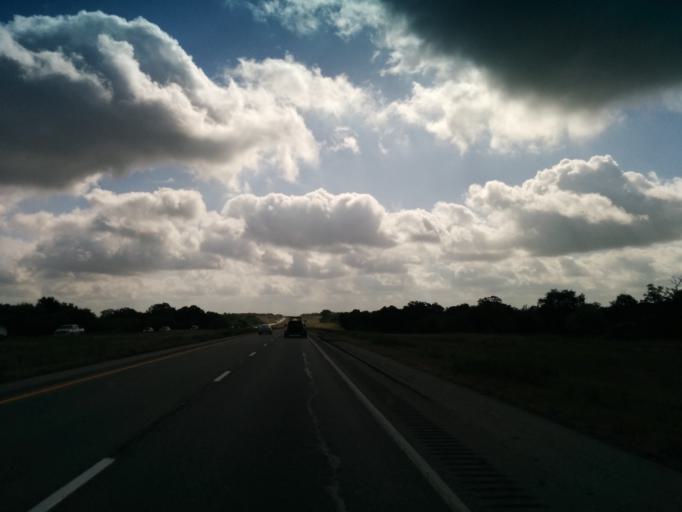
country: US
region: Texas
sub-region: Caldwell County
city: Luling
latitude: 29.6411
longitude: -97.7114
